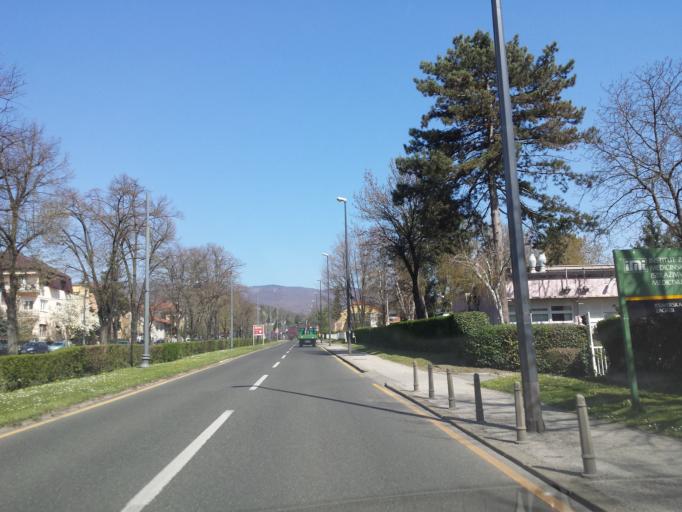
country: HR
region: Grad Zagreb
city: Zagreb
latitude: 45.8347
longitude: 15.9781
